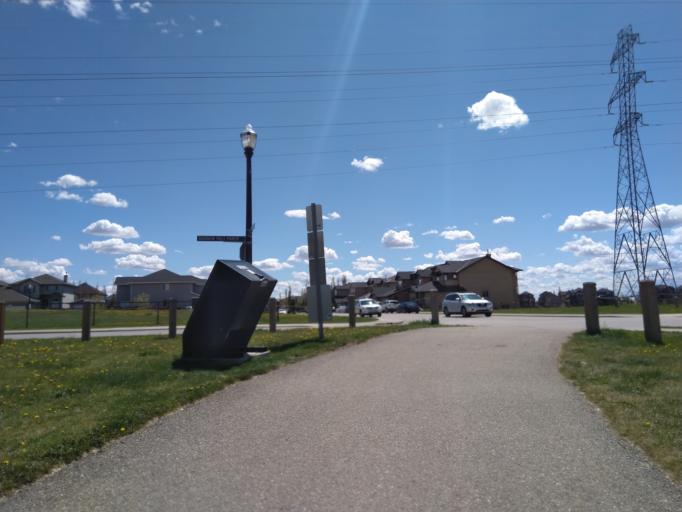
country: CA
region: Alberta
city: Chestermere
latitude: 51.0238
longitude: -113.8344
